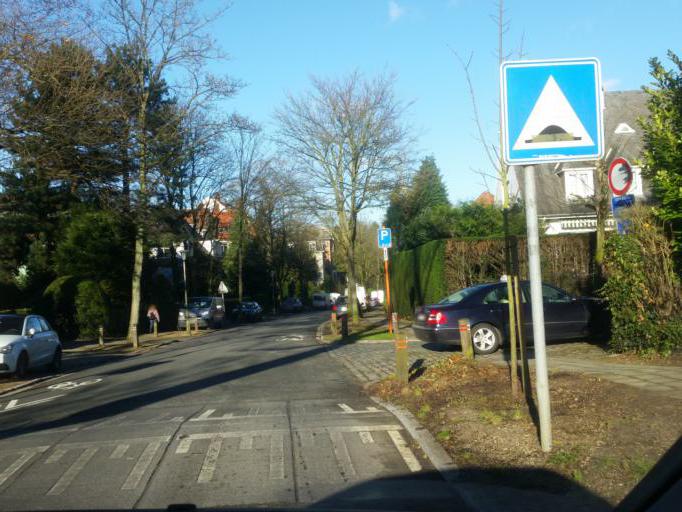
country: BE
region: Flanders
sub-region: Provincie Vlaams-Brabant
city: Linkebeek
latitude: 50.8015
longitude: 4.3625
